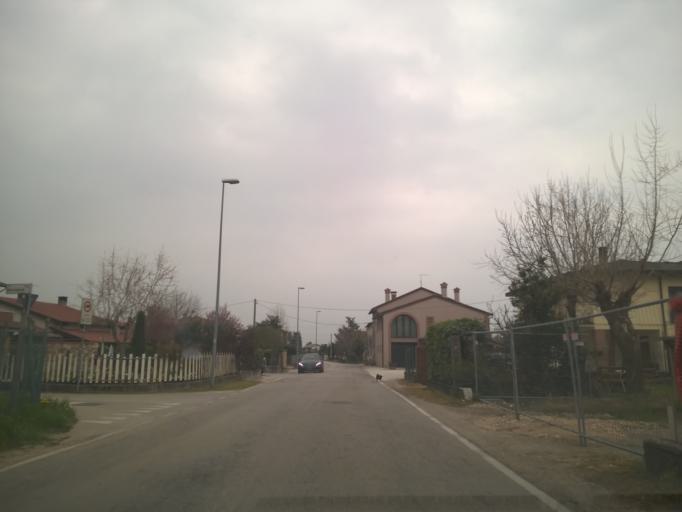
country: IT
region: Veneto
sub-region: Provincia di Vicenza
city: Sandrigo
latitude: 45.6513
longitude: 11.6004
